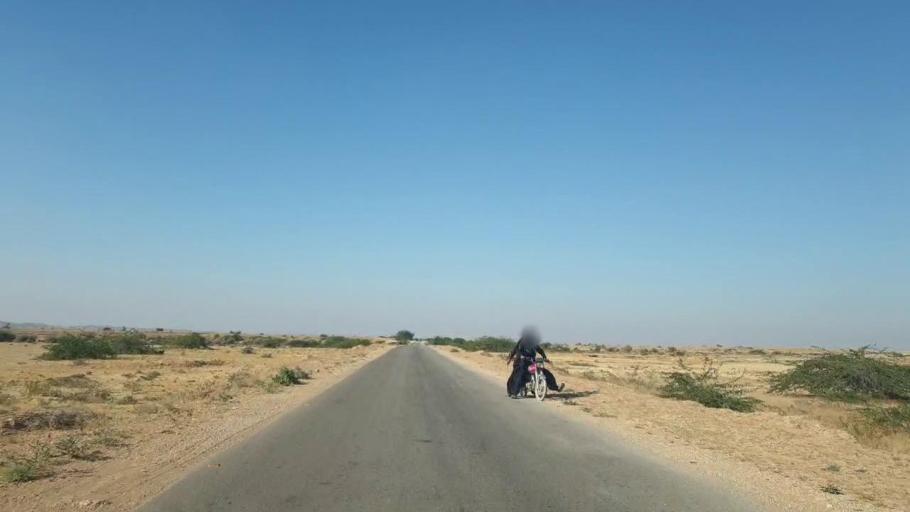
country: PK
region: Sindh
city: Malir Cantonment
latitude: 25.2539
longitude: 67.6026
